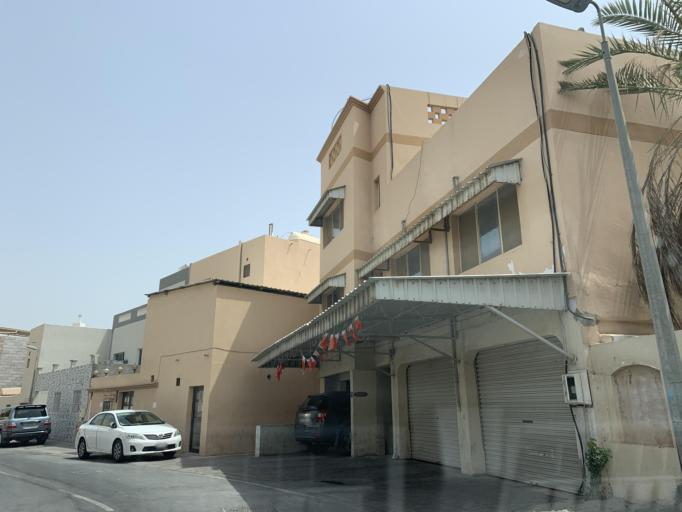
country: BH
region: Northern
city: Madinat `Isa
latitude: 26.1634
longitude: 50.5629
